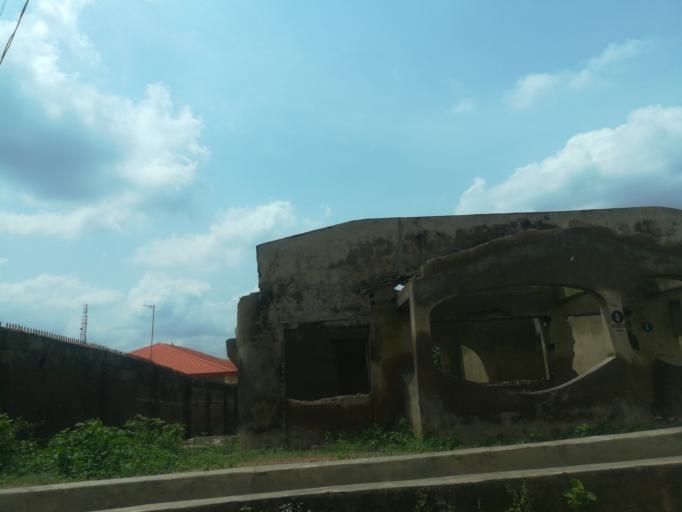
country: NG
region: Oyo
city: Moniya
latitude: 7.4517
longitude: 3.9553
